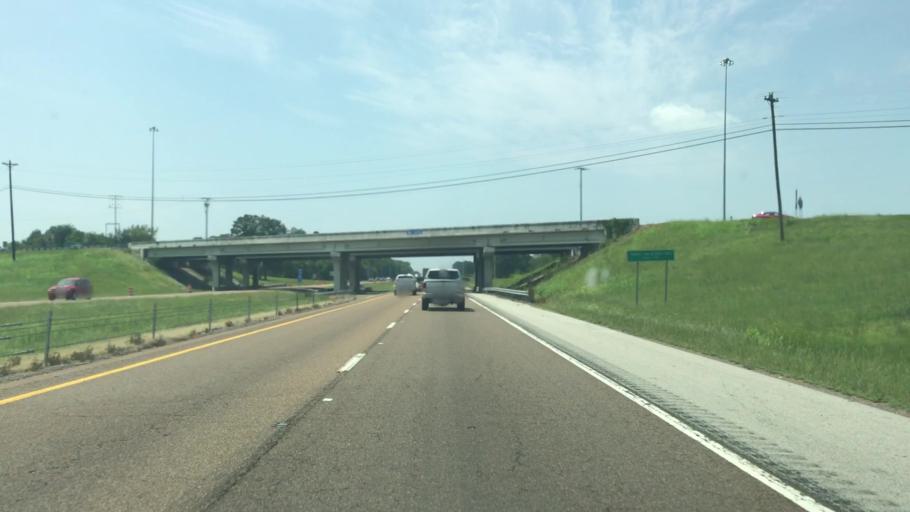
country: US
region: Tennessee
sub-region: Madison County
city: Jackson
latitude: 35.6812
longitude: -88.7413
